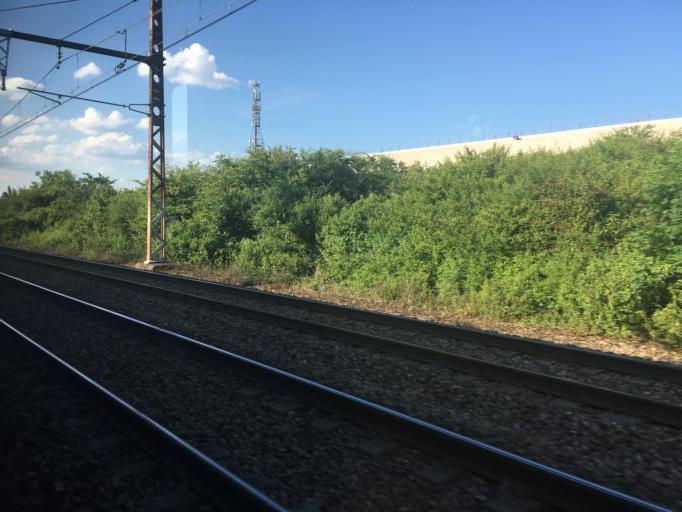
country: FR
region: Ile-de-France
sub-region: Departement de Seine-et-Marne
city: Moissy-Cramayel
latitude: 48.6179
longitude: 2.5741
